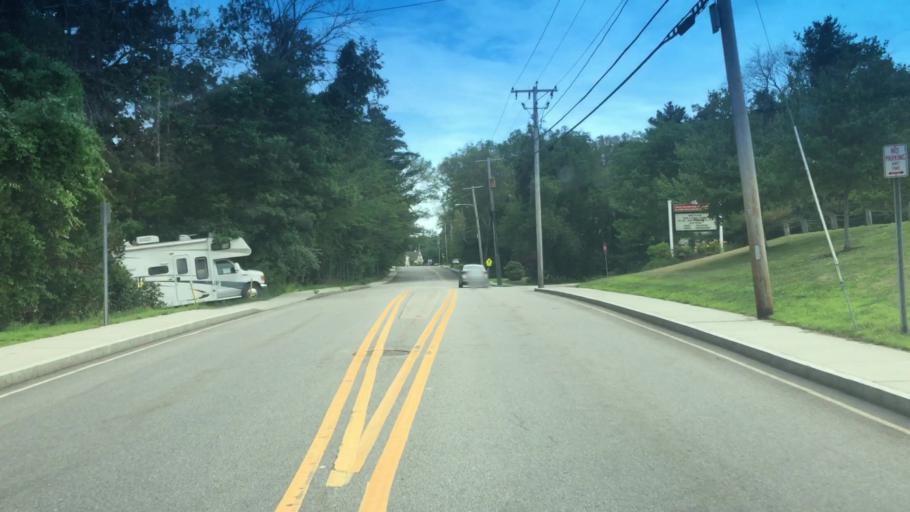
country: US
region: Massachusetts
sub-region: Norfolk County
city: Franklin
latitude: 42.1108
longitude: -71.3954
